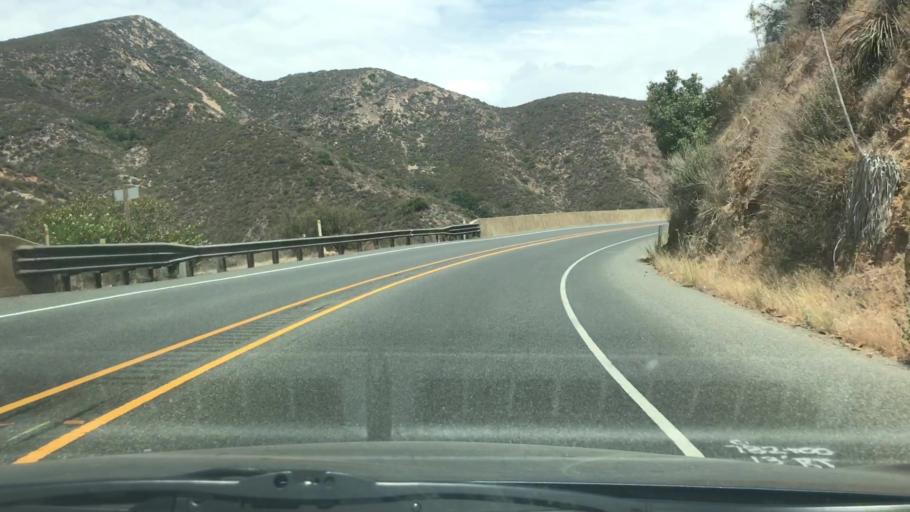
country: US
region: California
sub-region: Orange County
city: Coto De Caza
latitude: 33.5952
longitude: -117.4839
